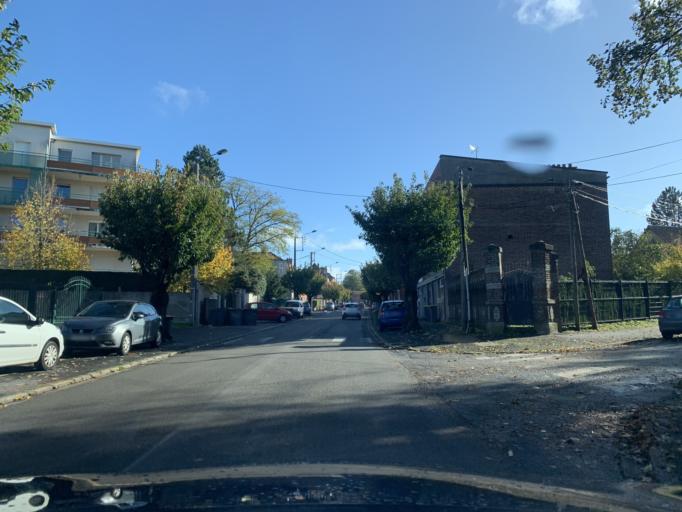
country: FR
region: Nord-Pas-de-Calais
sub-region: Departement du Nord
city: Cambrai
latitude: 50.1787
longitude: 3.2481
